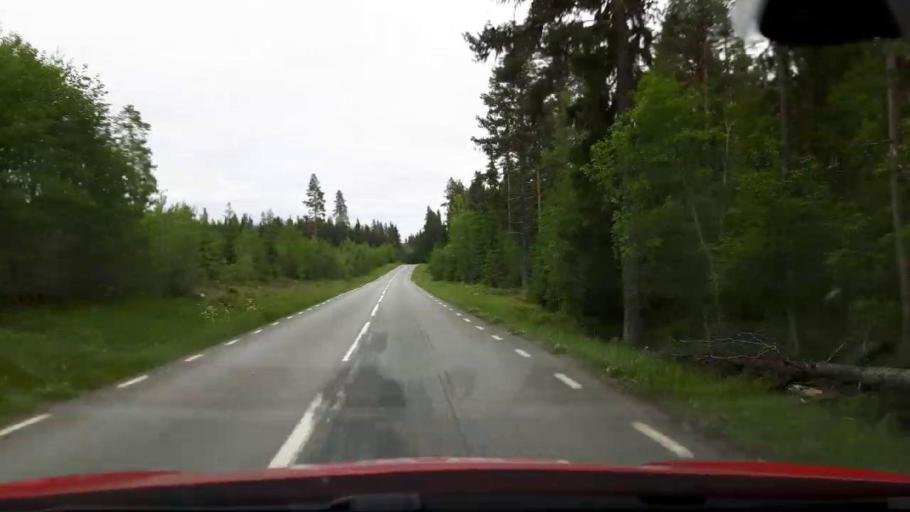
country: SE
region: Jaemtland
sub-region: Stroemsunds Kommun
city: Stroemsund
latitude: 63.4474
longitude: 15.4723
